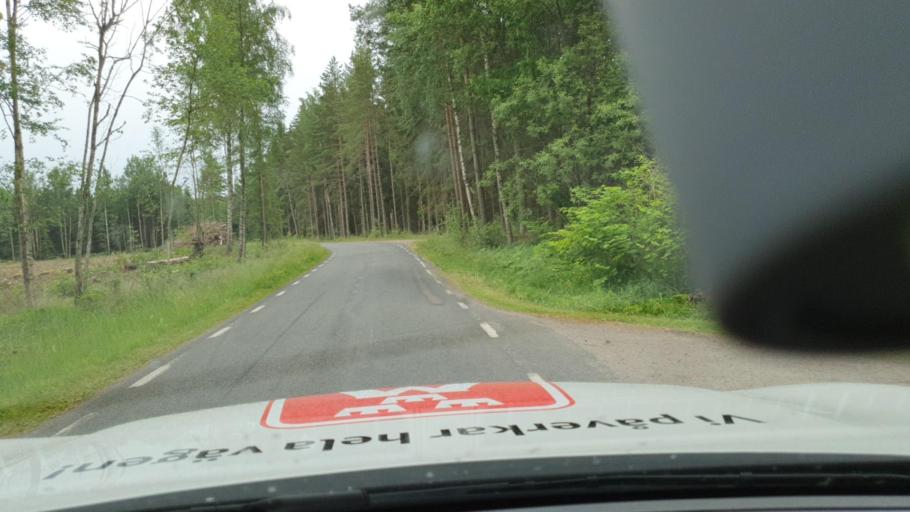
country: SE
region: Vaestra Goetaland
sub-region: Tibro Kommun
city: Tibro
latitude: 58.3257
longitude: 14.1844
